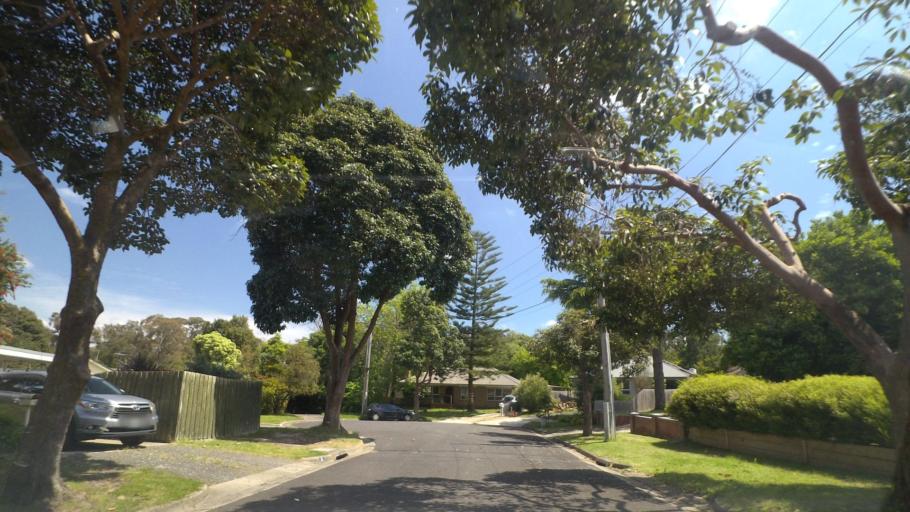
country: AU
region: Victoria
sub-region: Maroondah
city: Heathmont
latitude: -37.8276
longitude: 145.2564
